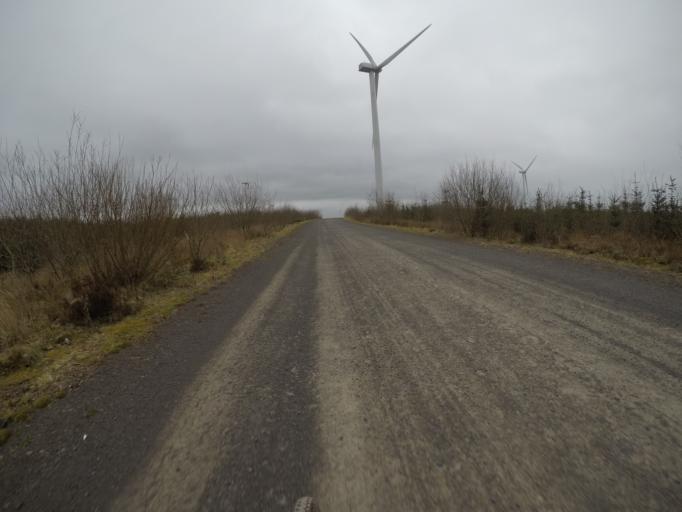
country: GB
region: Scotland
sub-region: East Ayrshire
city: Newmilns
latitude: 55.6563
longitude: -4.3246
